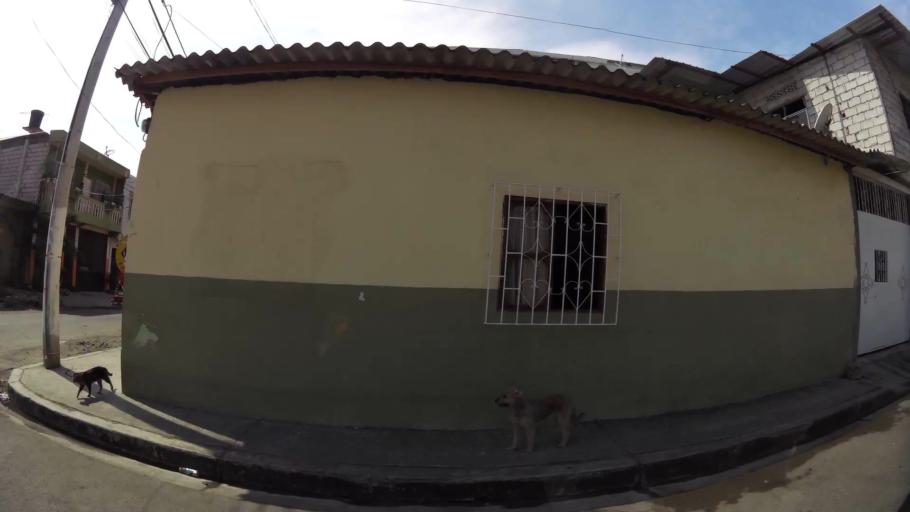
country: EC
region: Guayas
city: Guayaquil
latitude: -2.2617
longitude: -79.8835
